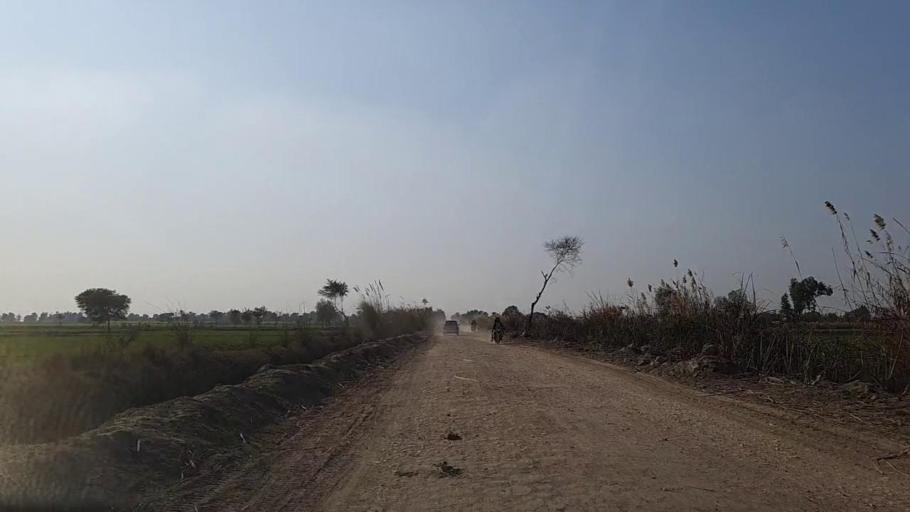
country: PK
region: Sindh
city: Daur
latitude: 26.4042
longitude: 68.2671
